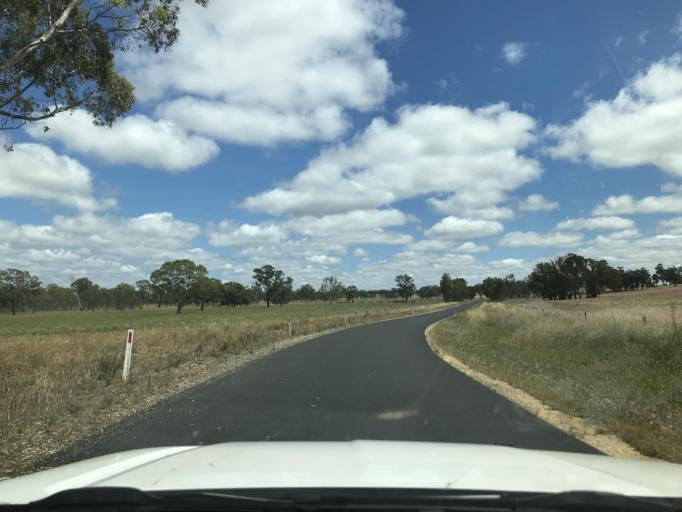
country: AU
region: South Australia
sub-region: Naracoorte and Lucindale
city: Naracoorte
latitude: -36.6815
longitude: 141.2981
